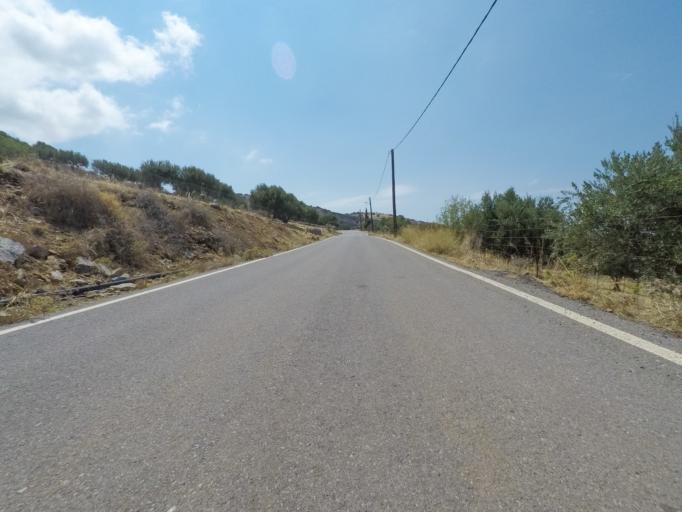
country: GR
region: Crete
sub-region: Nomos Lasithiou
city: Elounda
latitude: 35.3178
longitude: 25.6814
